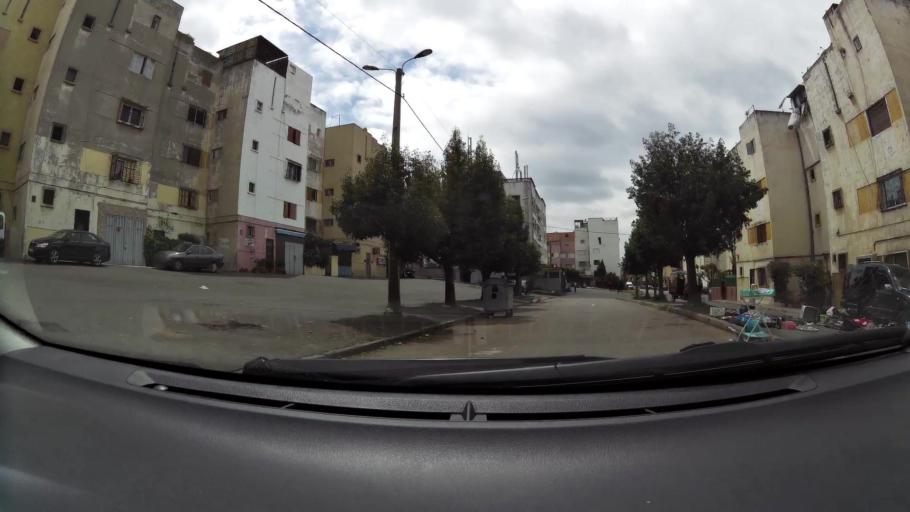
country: MA
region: Grand Casablanca
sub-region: Casablanca
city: Casablanca
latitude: 33.5772
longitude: -7.5610
